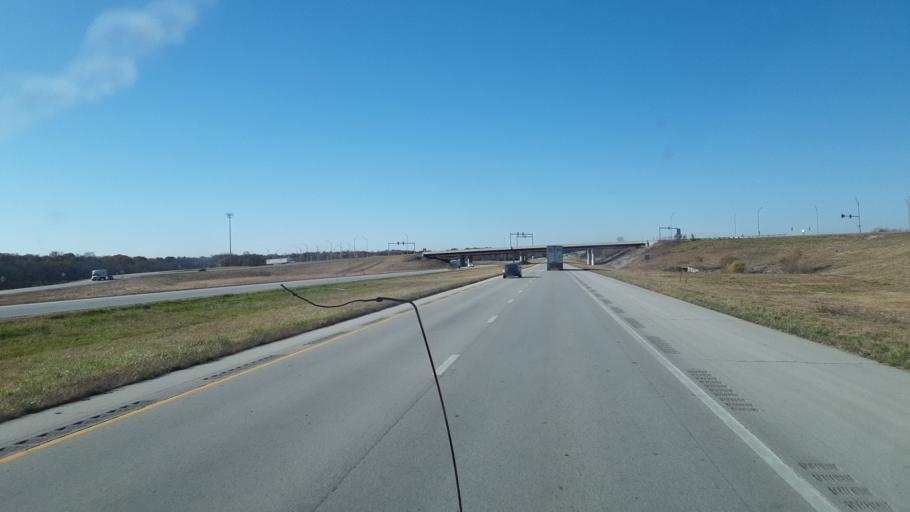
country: US
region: Kansas
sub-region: Johnson County
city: Edgerton
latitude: 38.7617
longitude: -94.9610
